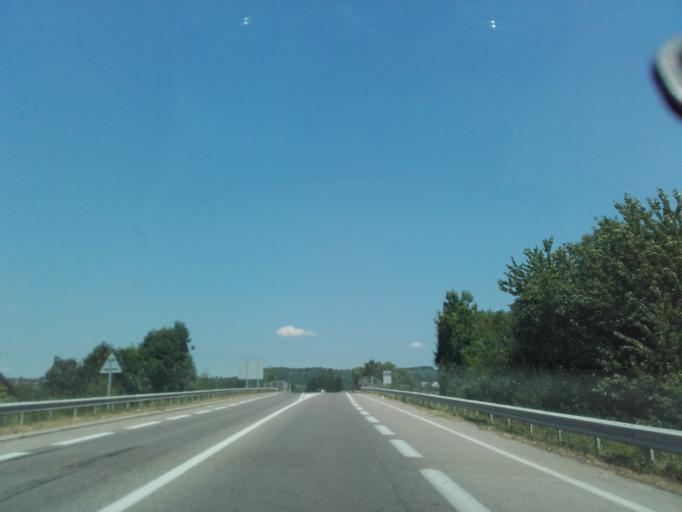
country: FR
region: Rhone-Alpes
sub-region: Departement de l'Isere
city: Bourgoin
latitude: 45.5752
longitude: 5.3018
